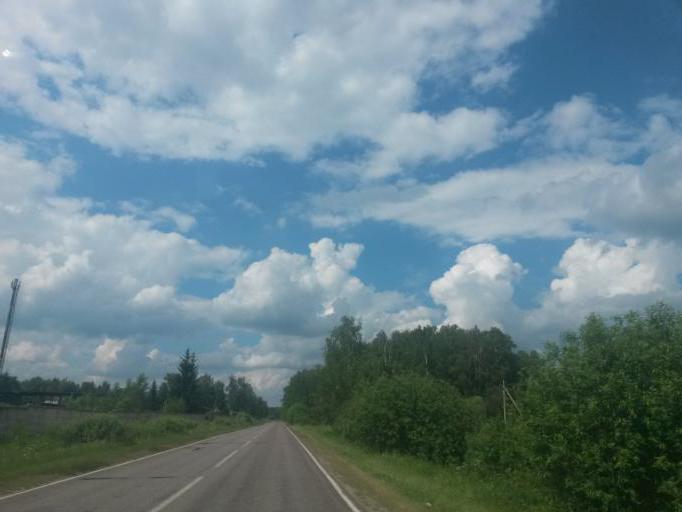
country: RU
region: Moskovskaya
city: Melikhovo
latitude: 55.2041
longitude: 37.6941
